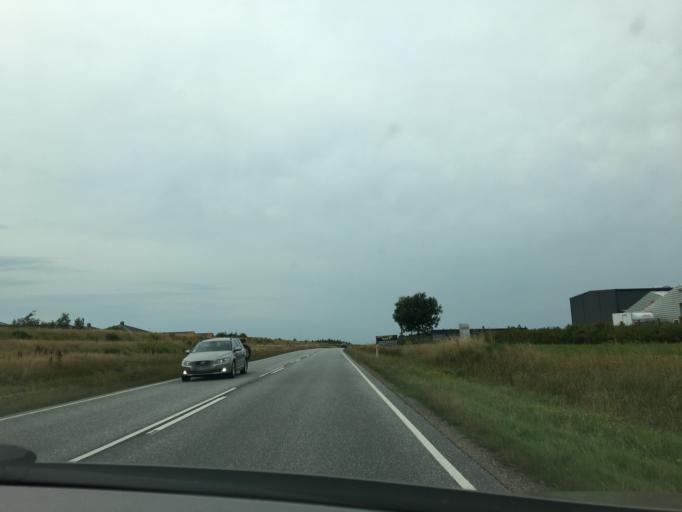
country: DK
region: Central Jutland
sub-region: Ringkobing-Skjern Kommune
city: Ringkobing
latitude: 56.0915
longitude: 8.2779
